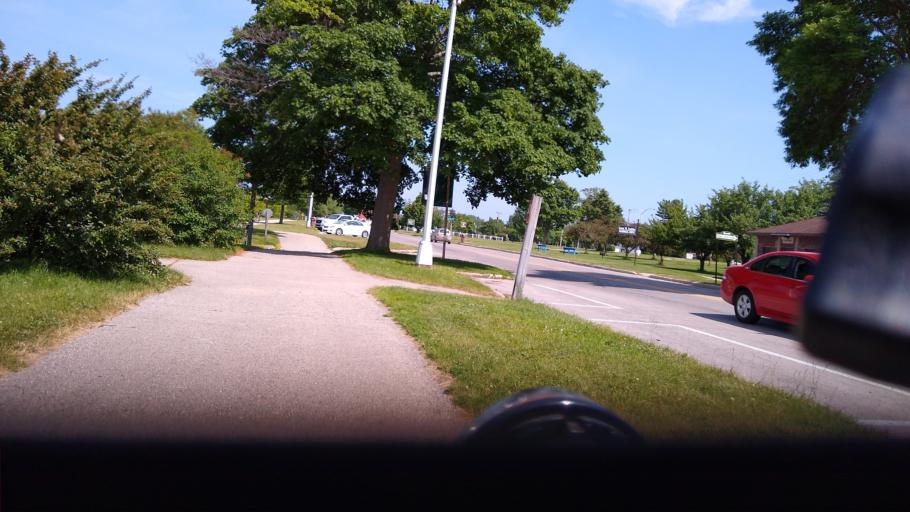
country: US
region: Michigan
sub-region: Delta County
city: Escanaba
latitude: 45.7456
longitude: -87.0471
